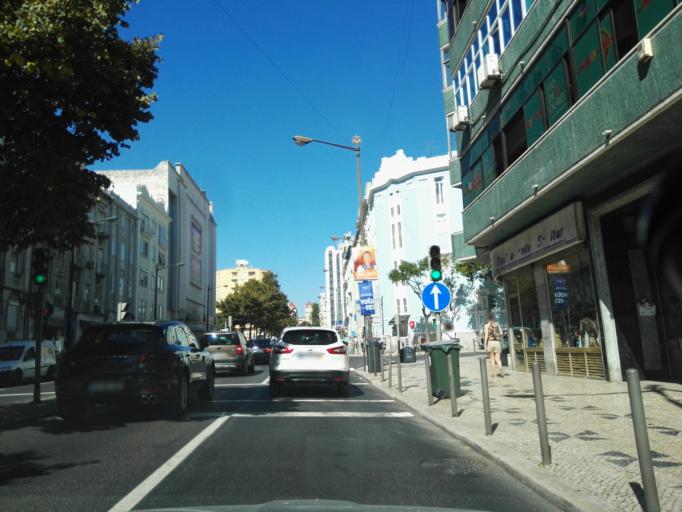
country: PT
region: Lisbon
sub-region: Lisbon
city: Lisbon
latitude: 38.7355
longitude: -9.1339
